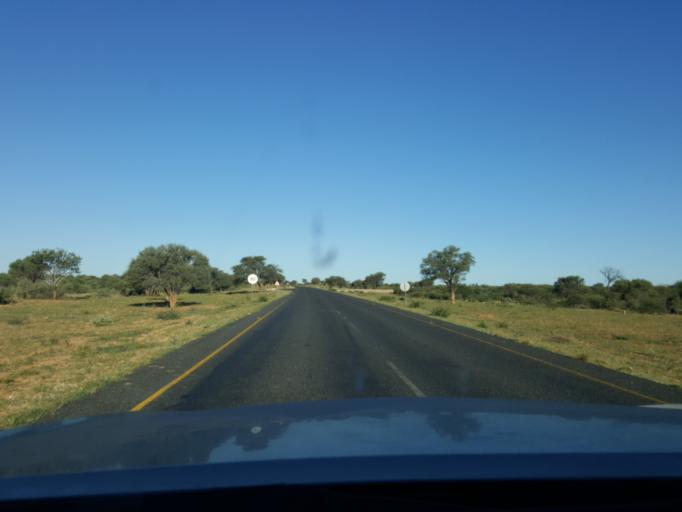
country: BW
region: Southern
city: Khakhea
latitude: -24.2287
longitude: 23.2436
